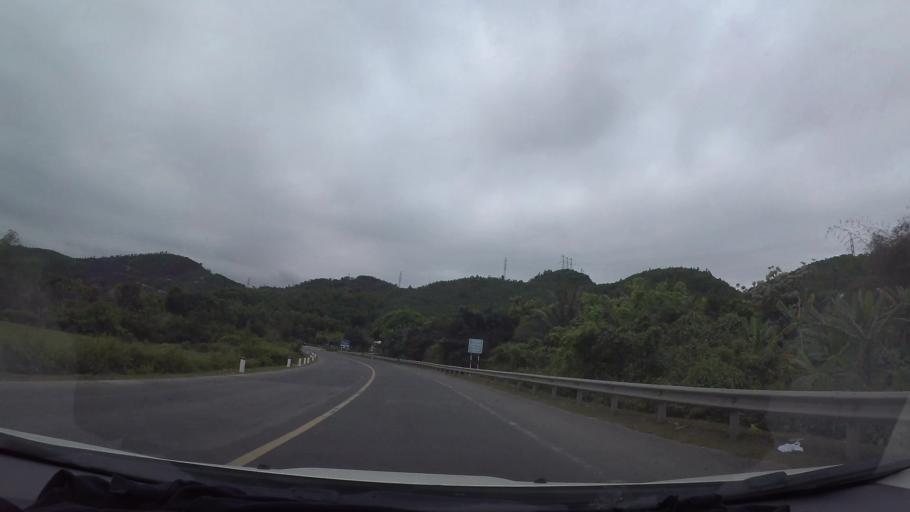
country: VN
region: Da Nang
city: Lien Chieu
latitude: 16.1287
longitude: 108.1003
